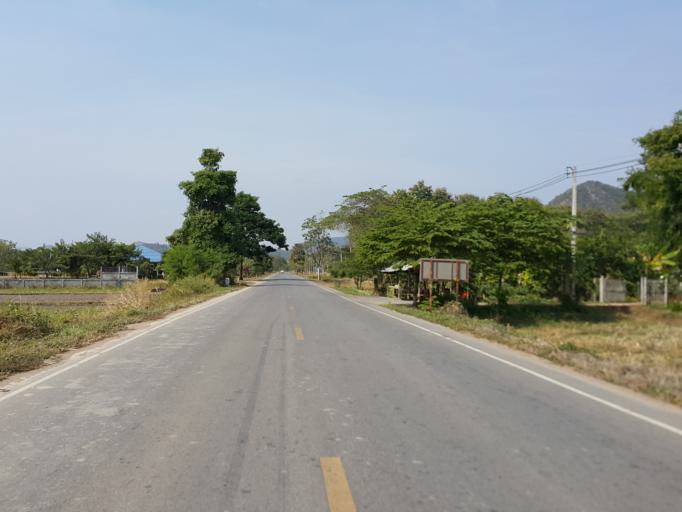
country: TH
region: Sukhothai
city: Thung Saliam
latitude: 17.3315
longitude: 99.4992
